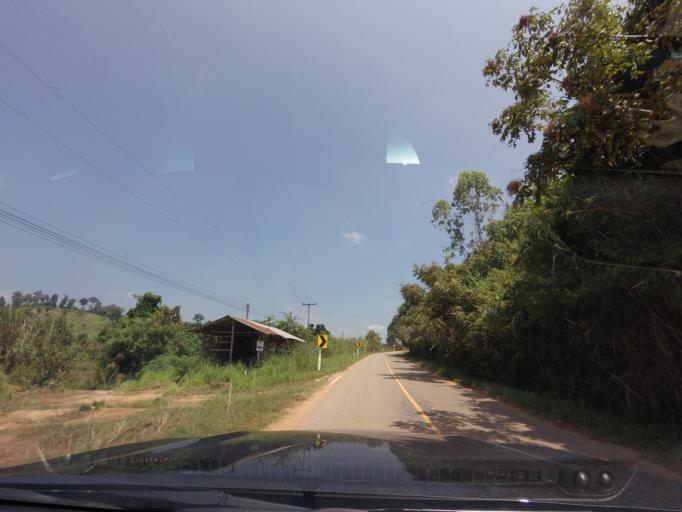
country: TH
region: Loei
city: Na Haeo
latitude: 17.5485
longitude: 100.8787
